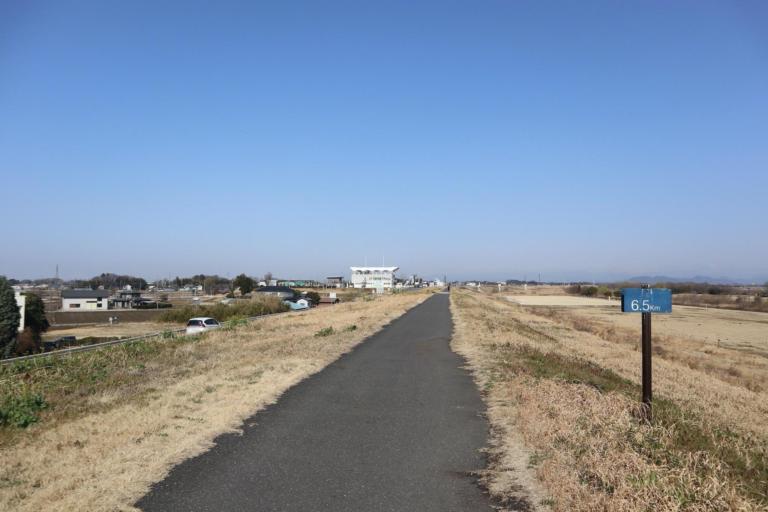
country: JP
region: Tochigi
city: Fujioka
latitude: 36.2094
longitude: 139.6650
